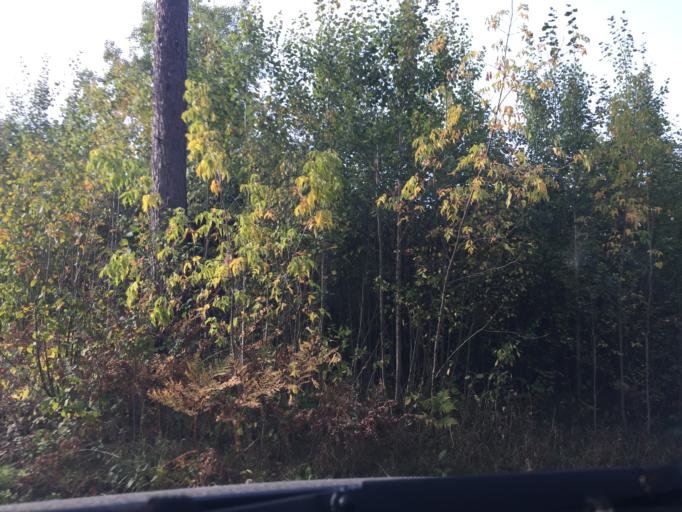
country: LV
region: Garkalne
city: Garkalne
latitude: 56.9738
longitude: 24.4319
